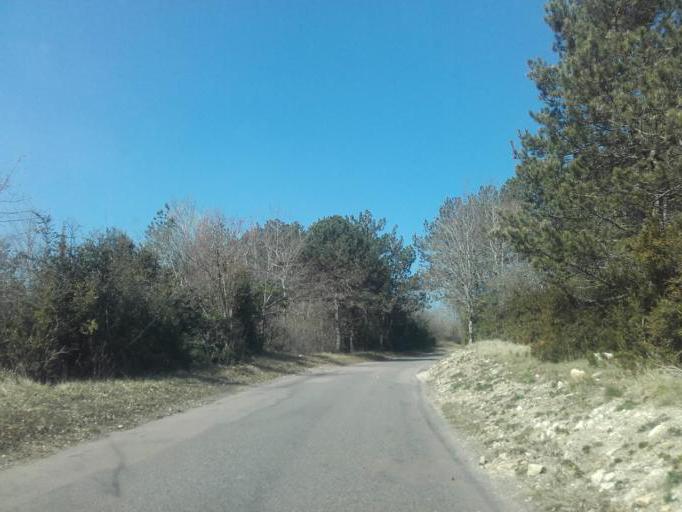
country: FR
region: Bourgogne
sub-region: Departement de la Cote-d'Or
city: Savigny-les-Beaune
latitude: 47.0576
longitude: 4.7845
